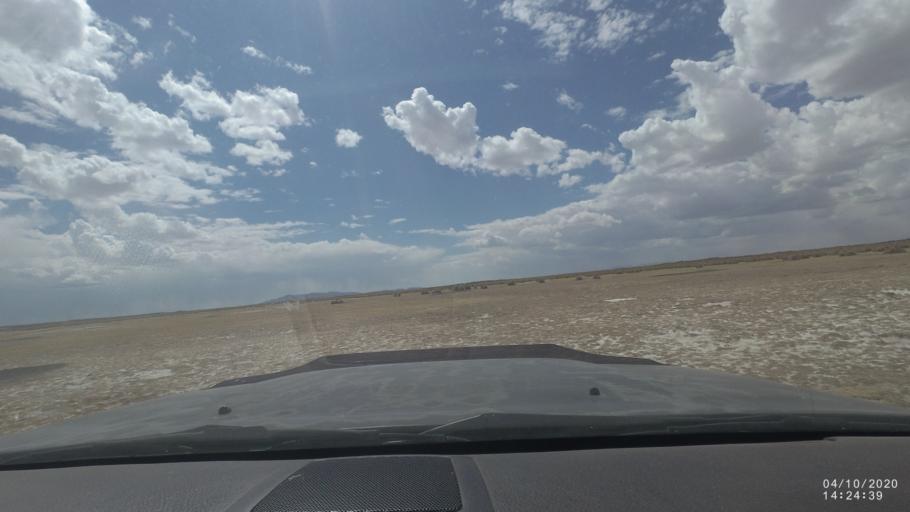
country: BO
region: Oruro
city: Poopo
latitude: -18.6763
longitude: -67.4507
